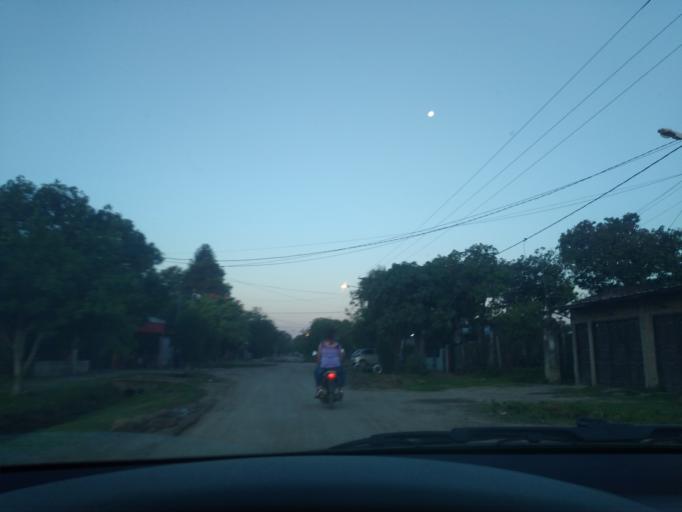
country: AR
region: Chaco
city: Barranqueras
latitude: -27.4755
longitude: -58.9331
